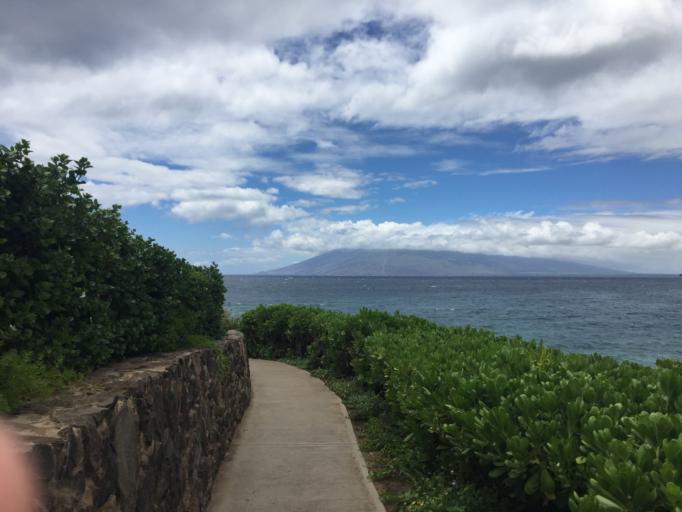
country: US
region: Hawaii
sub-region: Maui County
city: Kihei
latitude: 20.6808
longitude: -156.4441
